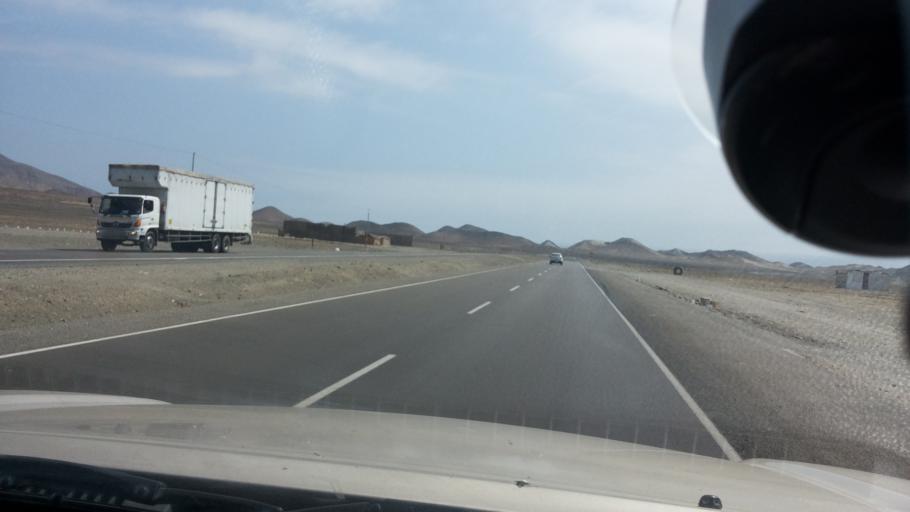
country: PE
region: Ancash
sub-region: Provincia de Huarmey
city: La Caleta Culebras
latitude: -9.8726
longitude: -78.2107
